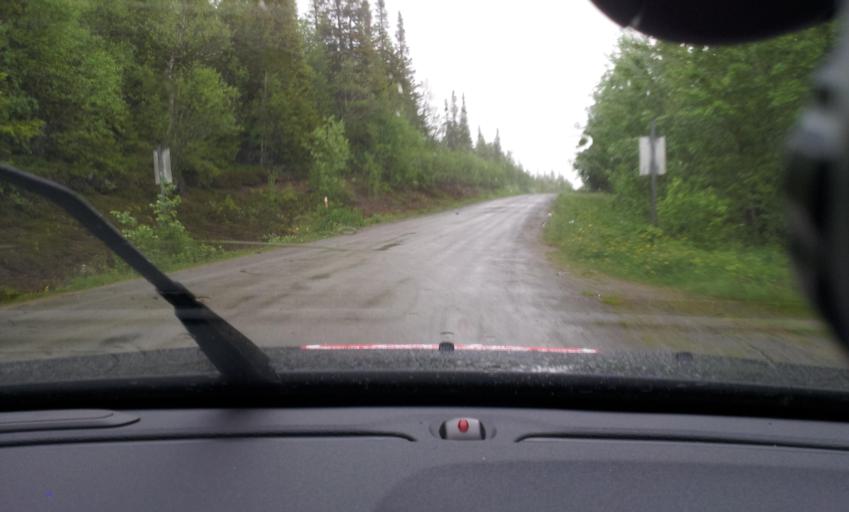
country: SE
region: Jaemtland
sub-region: Are Kommun
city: Are
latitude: 63.2197
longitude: 13.0510
